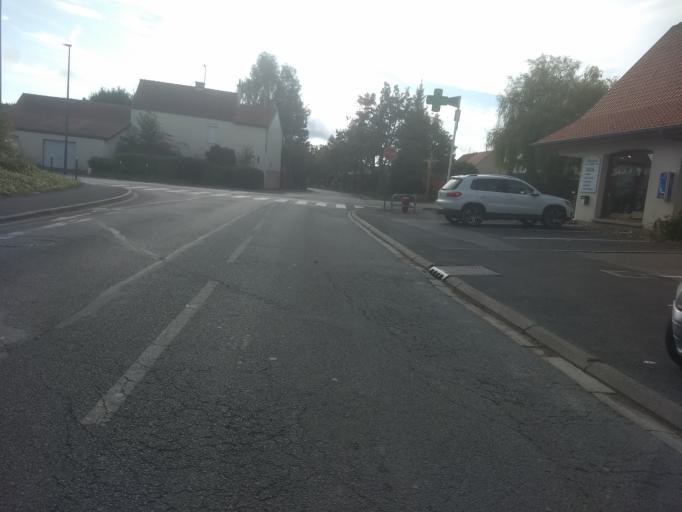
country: FR
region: Nord-Pas-de-Calais
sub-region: Departement du Pas-de-Calais
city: Dainville
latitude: 50.2789
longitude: 2.7190
